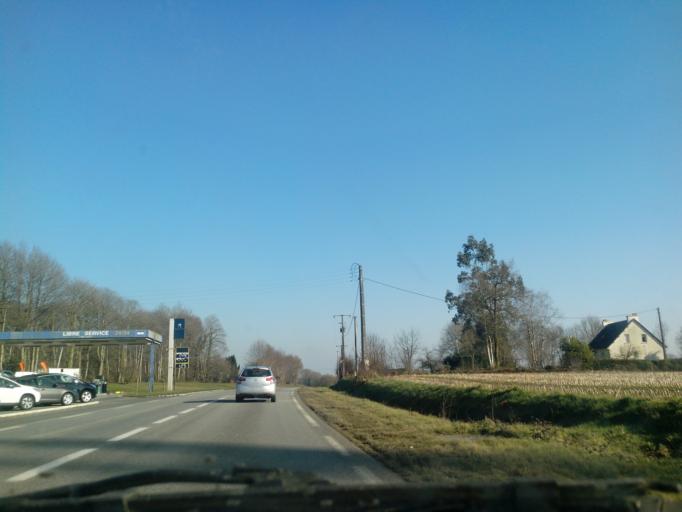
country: FR
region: Brittany
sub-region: Departement du Morbihan
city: Meneac
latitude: 48.1987
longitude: -2.4818
